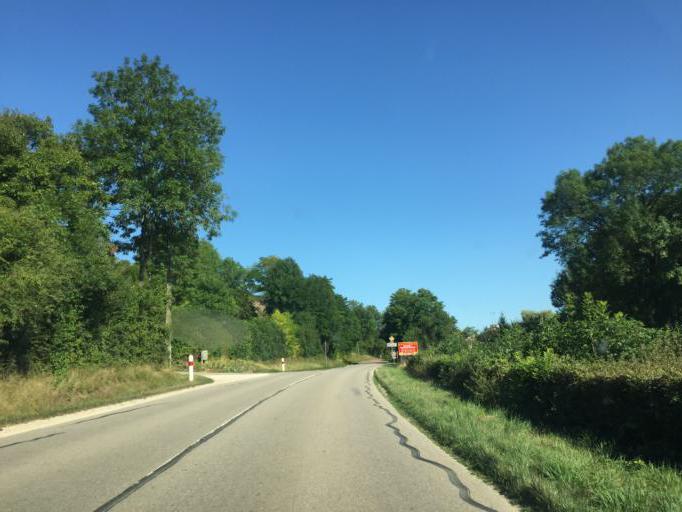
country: FR
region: Bourgogne
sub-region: Departement de la Nievre
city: Clamecy
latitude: 47.4566
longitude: 3.4656
